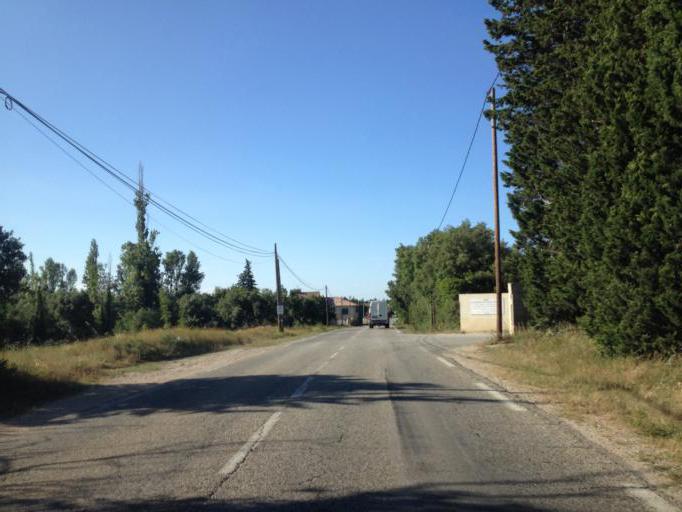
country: FR
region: Provence-Alpes-Cote d'Azur
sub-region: Departement du Vaucluse
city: Caderousse
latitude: 44.1047
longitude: 4.7911
